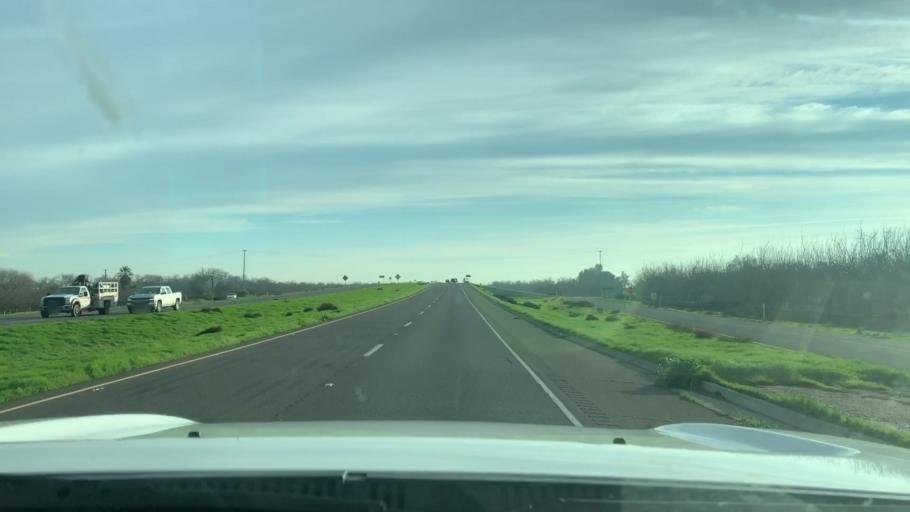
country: US
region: California
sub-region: Fresno County
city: Riverdale
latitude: 36.4049
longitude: -119.8066
